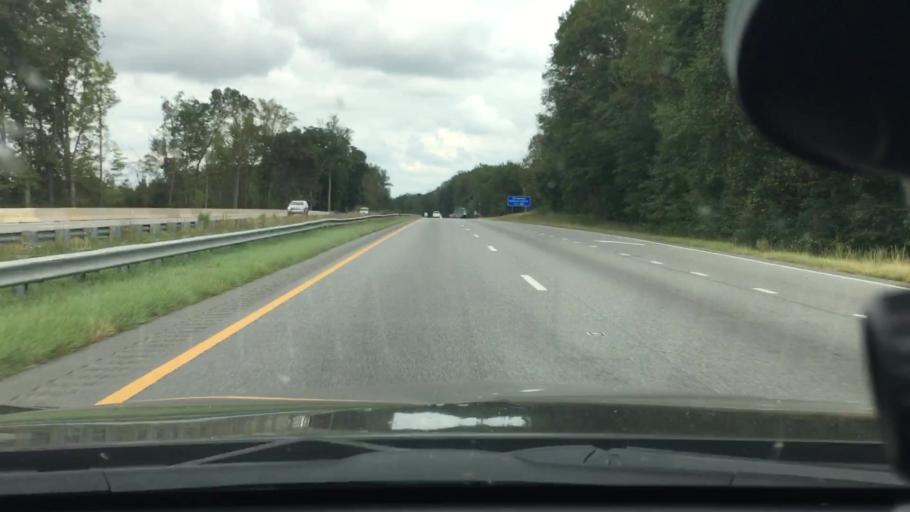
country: US
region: North Carolina
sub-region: Davie County
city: Bermuda Run
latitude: 36.0081
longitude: -80.4380
